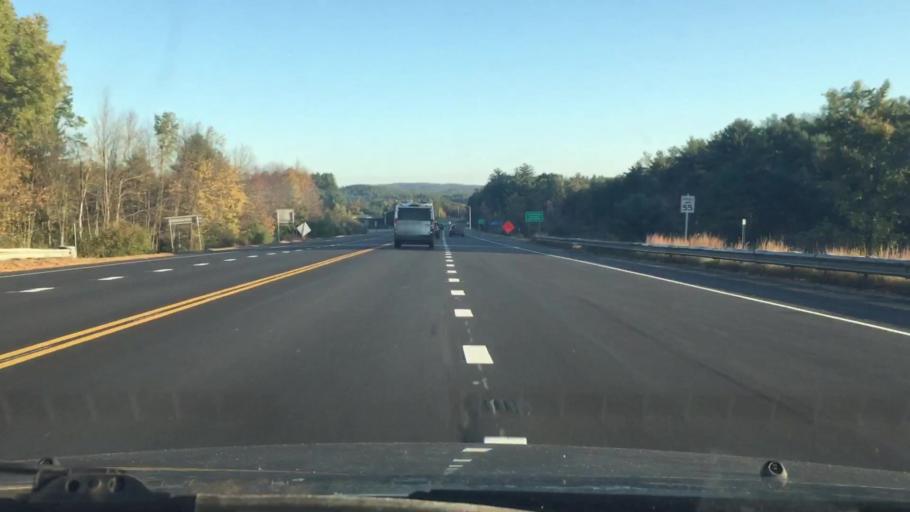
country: US
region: New Hampshire
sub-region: Cheshire County
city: Keene
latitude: 42.9378
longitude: -72.2964
